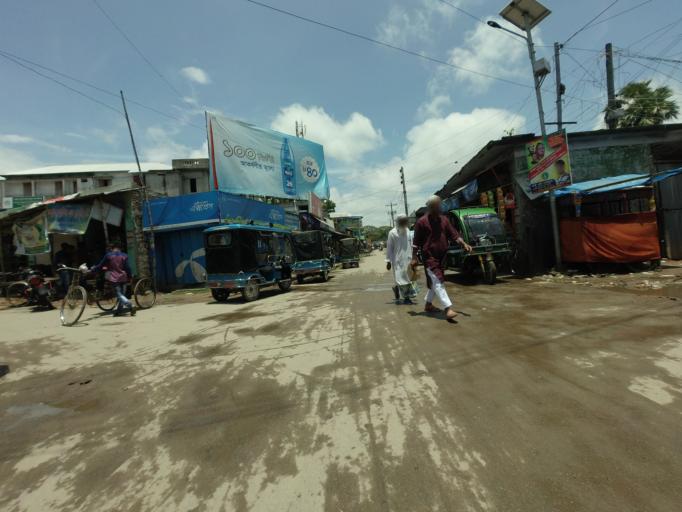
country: BD
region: Khulna
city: Kalia
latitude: 23.0408
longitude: 89.6309
